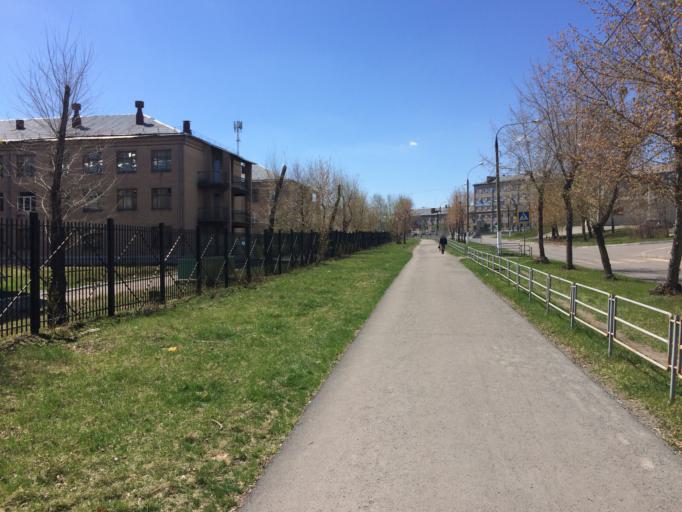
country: RU
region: Chelyabinsk
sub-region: Gorod Magnitogorsk
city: Magnitogorsk
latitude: 53.4041
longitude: 58.9640
